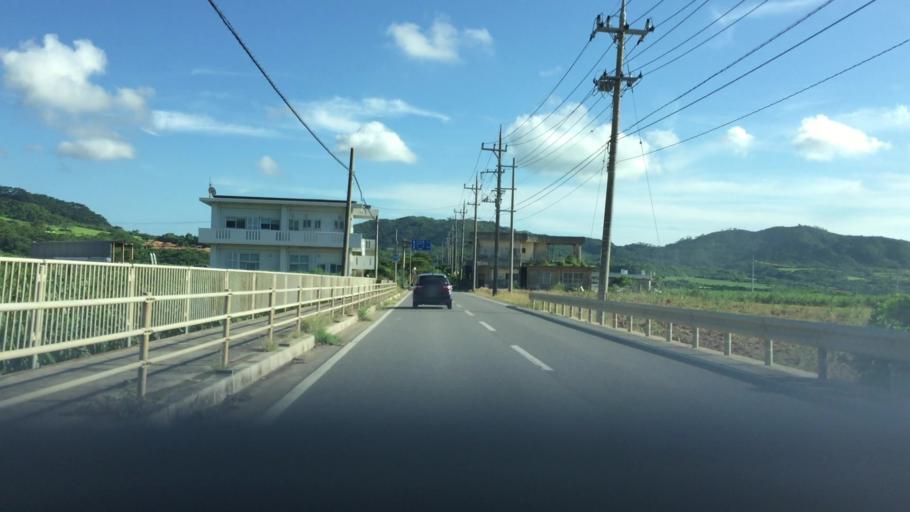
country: JP
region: Okinawa
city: Ishigaki
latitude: 24.3937
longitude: 124.1559
